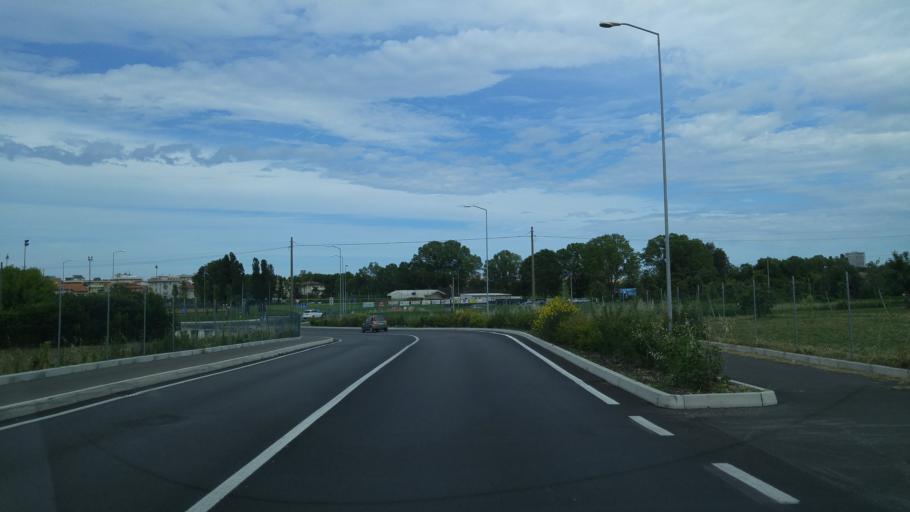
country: IT
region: Emilia-Romagna
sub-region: Provincia di Rimini
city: Rimini
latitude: 44.0748
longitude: 12.5465
